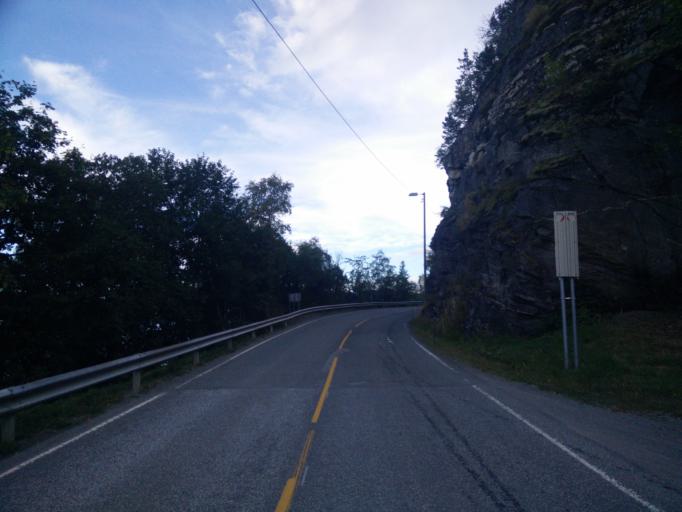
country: NO
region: Sor-Trondelag
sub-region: Skaun
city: Borsa
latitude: 63.3247
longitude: 10.0817
